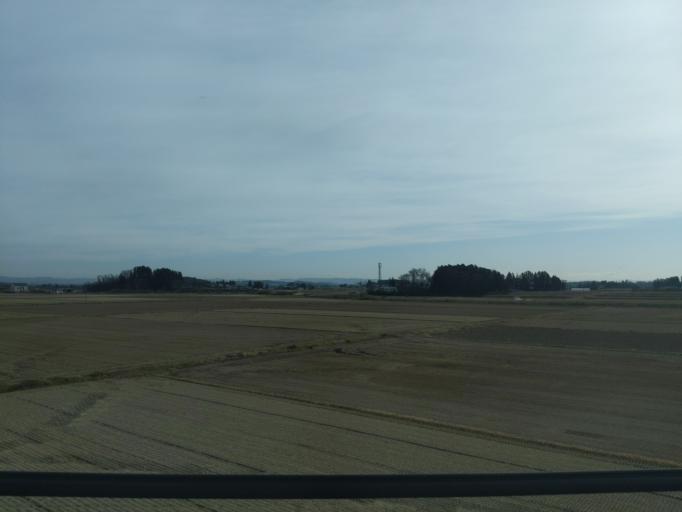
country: JP
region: Iwate
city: Ichinoseki
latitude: 38.7781
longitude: 141.0884
